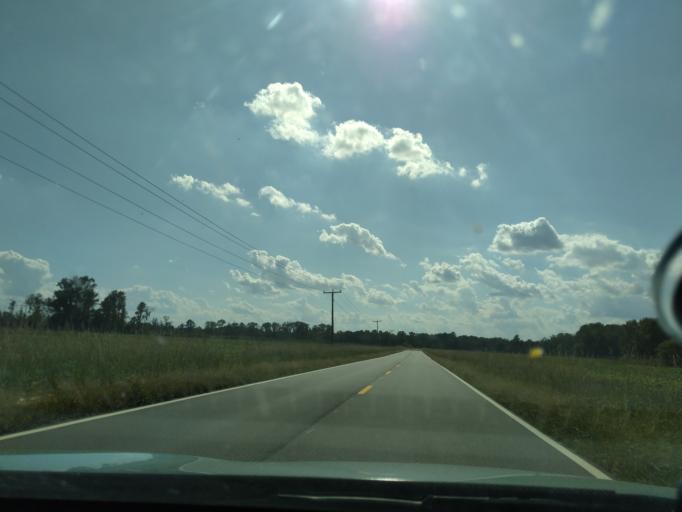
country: US
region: North Carolina
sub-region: Pitt County
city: Bethel
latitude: 35.8143
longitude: -77.3484
